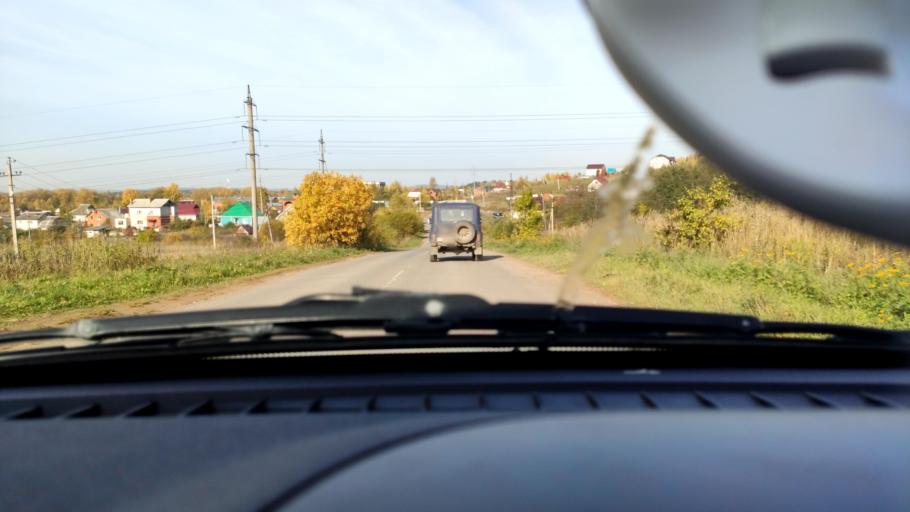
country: RU
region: Perm
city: Overyata
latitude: 58.0805
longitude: 55.8862
